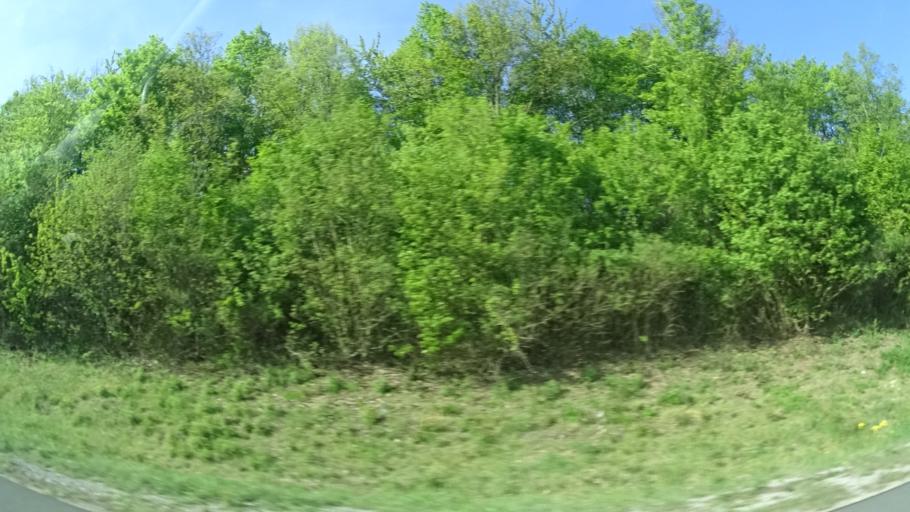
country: DE
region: Bavaria
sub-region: Regierungsbezirk Unterfranken
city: Gadheim
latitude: 50.0076
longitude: 10.3728
